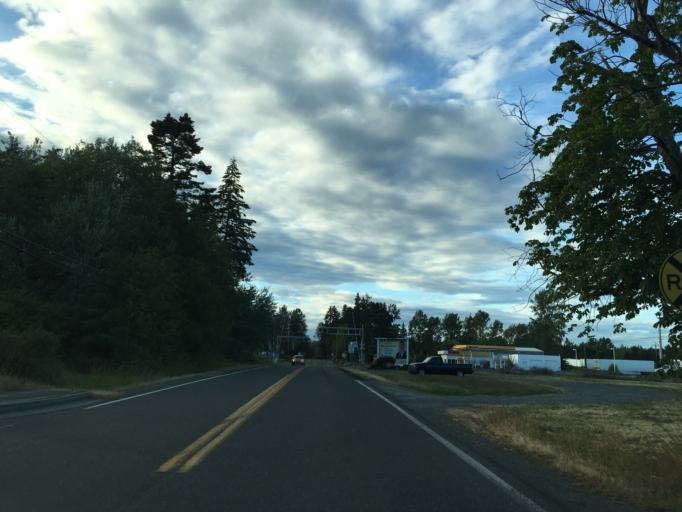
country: US
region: Washington
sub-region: Whatcom County
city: Blaine
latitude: 48.9743
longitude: -122.7284
